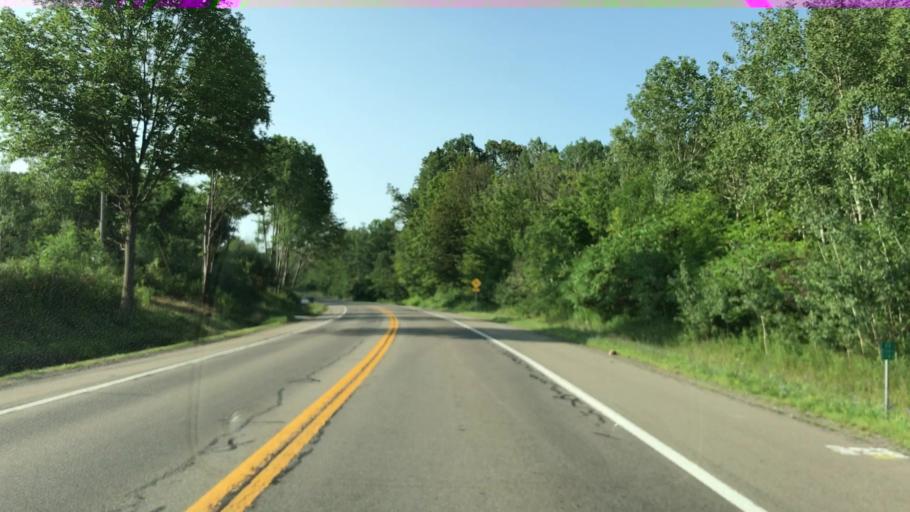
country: US
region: New York
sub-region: Chautauqua County
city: Fredonia
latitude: 42.3728
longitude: -79.3144
